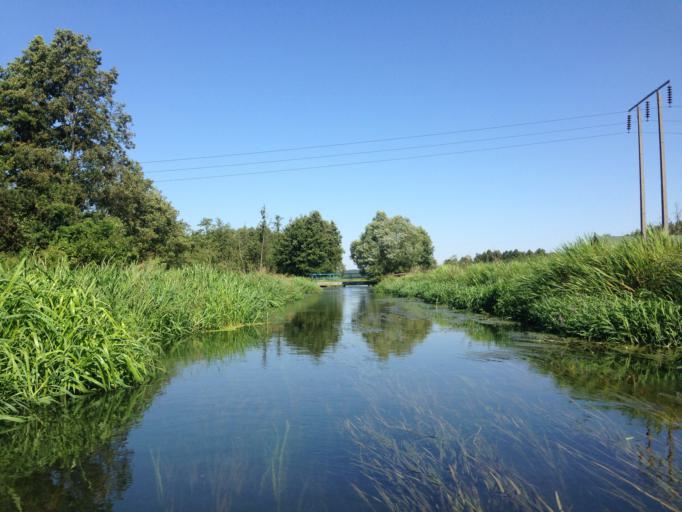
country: PL
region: Kujawsko-Pomorskie
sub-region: Powiat brodnicki
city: Bartniczka
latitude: 53.2591
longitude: 19.6006
